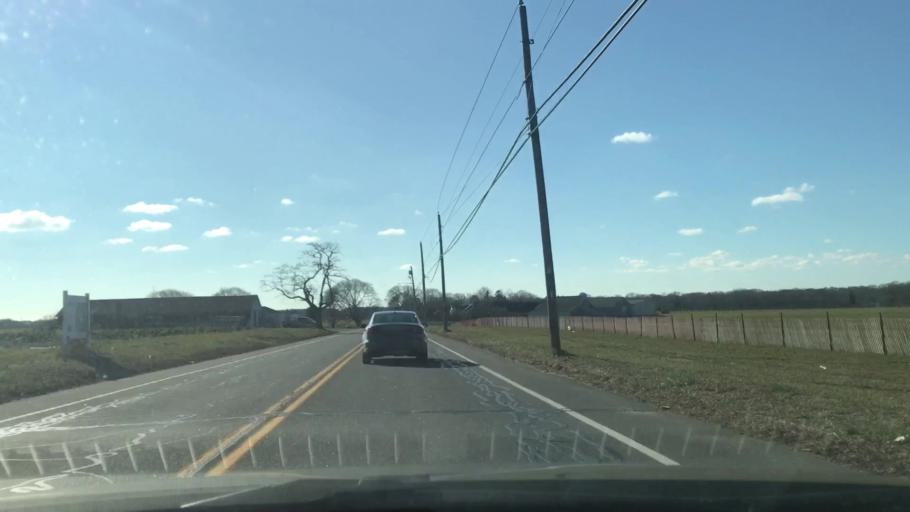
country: US
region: New York
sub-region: Suffolk County
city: Aquebogue
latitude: 40.9554
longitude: -72.6529
